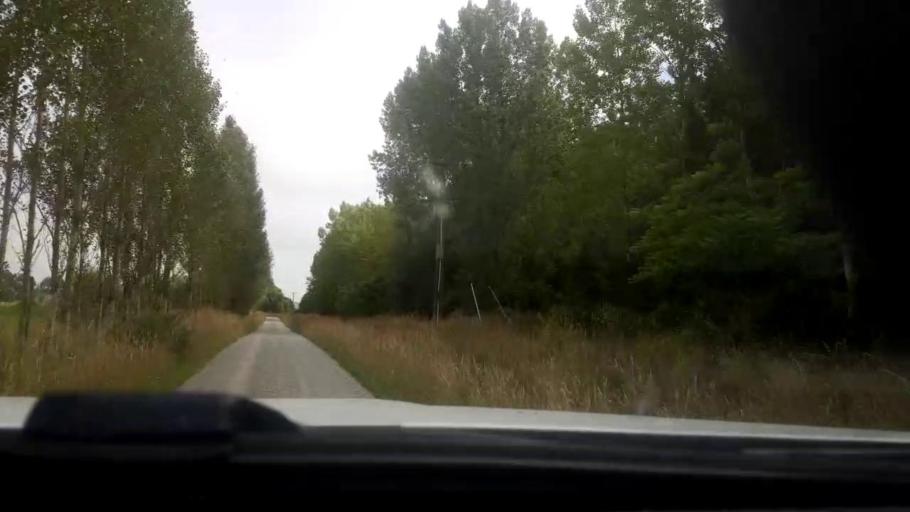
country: NZ
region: Canterbury
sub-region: Timaru District
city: Pleasant Point
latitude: -44.3272
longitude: 171.1965
